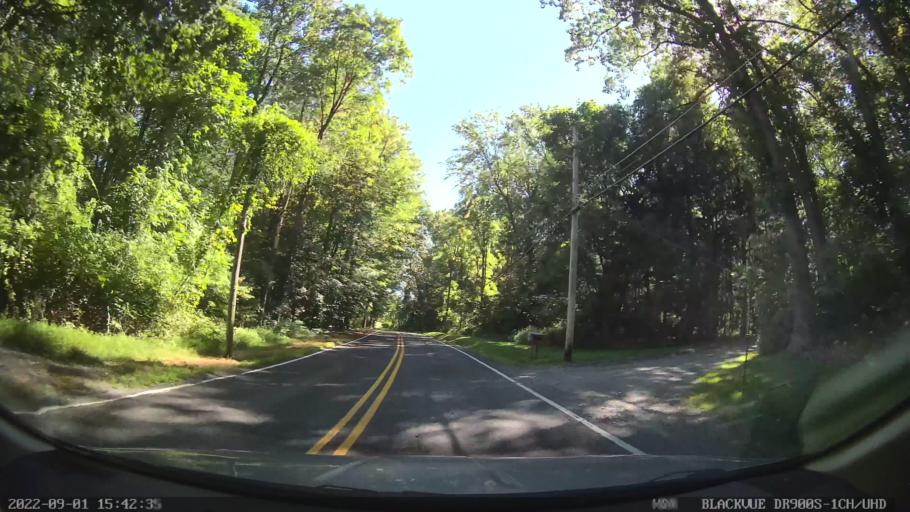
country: US
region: Pennsylvania
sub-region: Berks County
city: Topton
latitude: 40.4893
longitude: -75.7009
